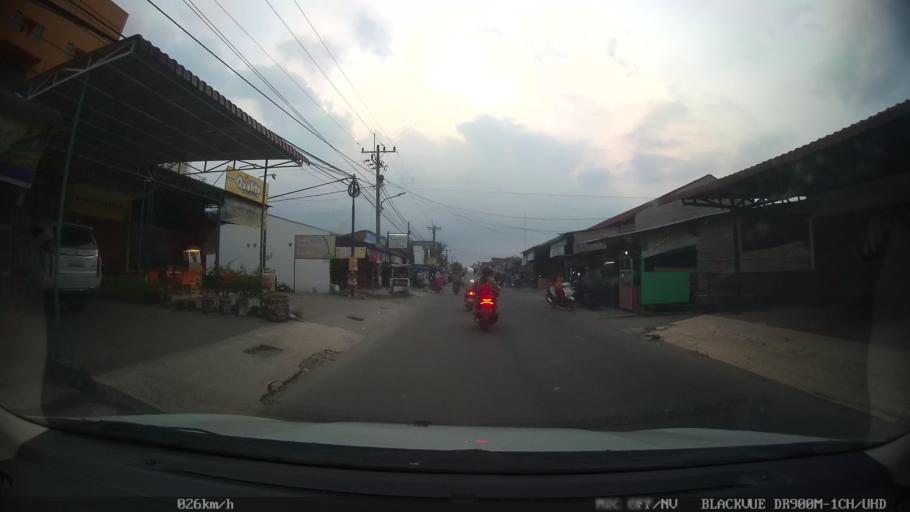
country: ID
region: North Sumatra
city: Sunggal
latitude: 3.5641
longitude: 98.6003
